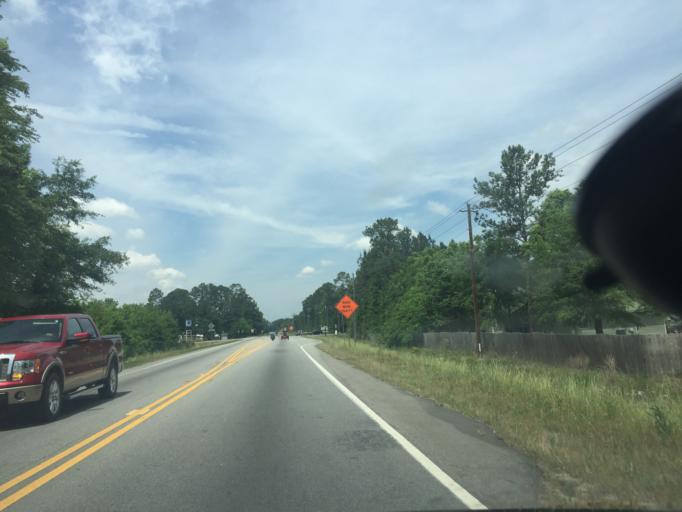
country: US
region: Georgia
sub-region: Chatham County
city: Bloomingdale
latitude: 32.1831
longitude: -81.3989
